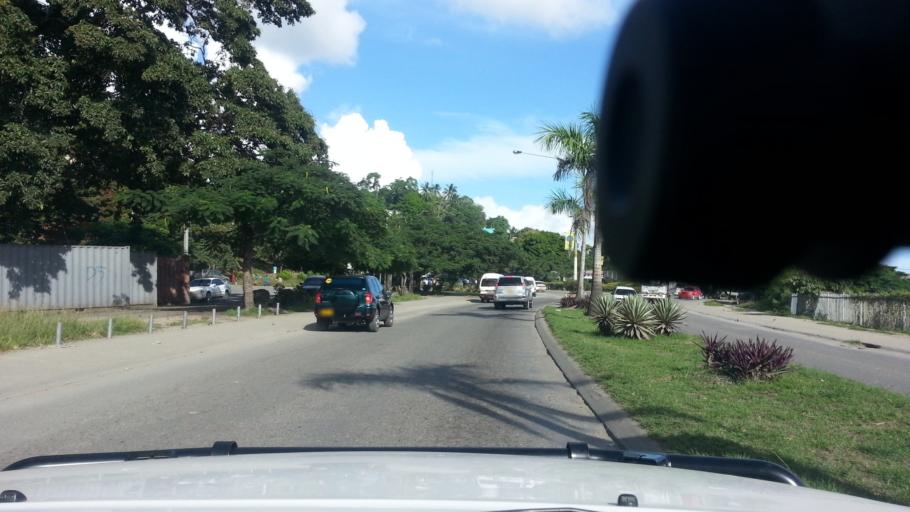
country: SB
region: Guadalcanal
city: Honiara
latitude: -9.4360
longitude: 159.9650
